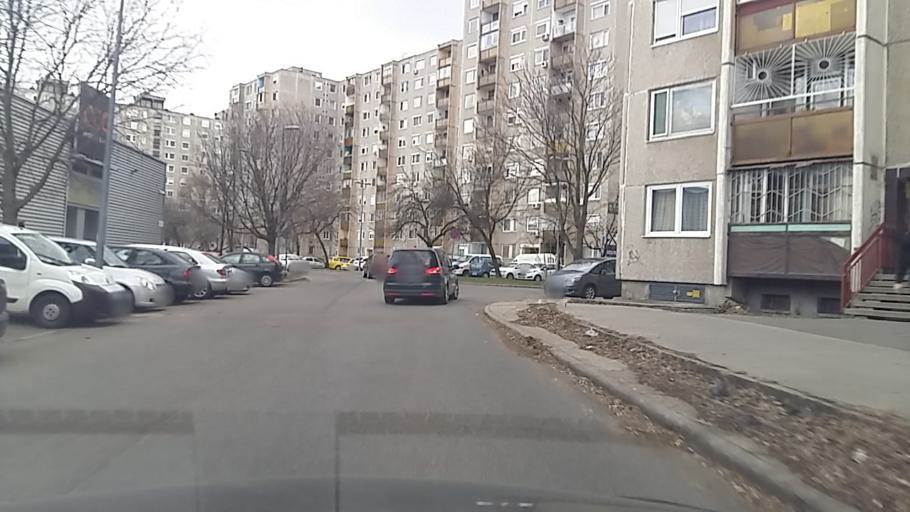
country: HU
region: Budapest
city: Budapest XV. keruelet
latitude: 47.5612
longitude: 19.1056
